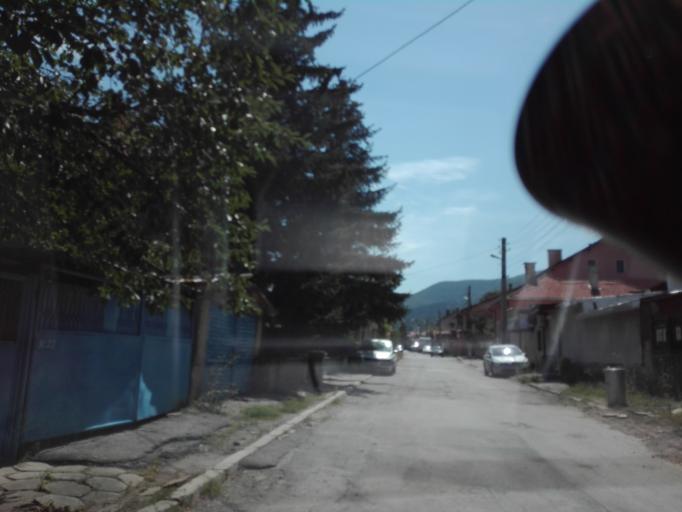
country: BG
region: Sofiya
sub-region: Obshtina Elin Pelin
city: Elin Pelin
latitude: 42.6061
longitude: 23.4718
